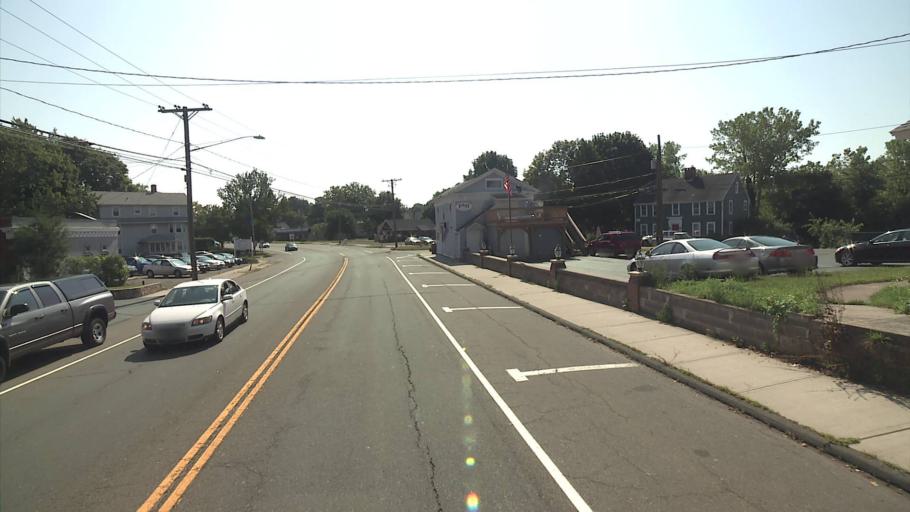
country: US
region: Connecticut
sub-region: New Haven County
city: Branford Center
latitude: 41.2773
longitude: -72.8207
